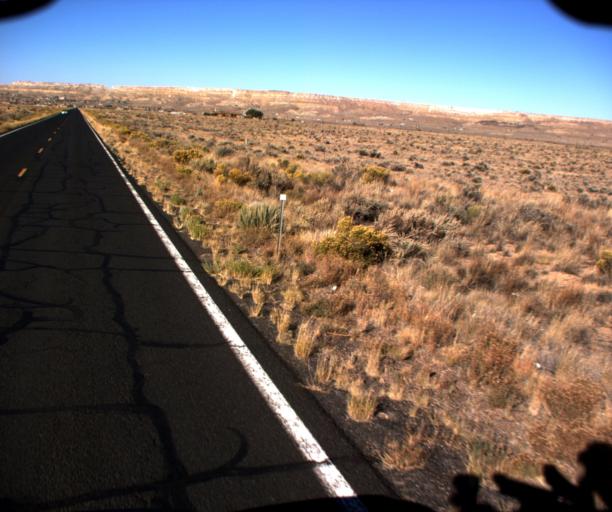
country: US
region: Arizona
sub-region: Navajo County
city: First Mesa
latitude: 35.8414
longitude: -110.3352
